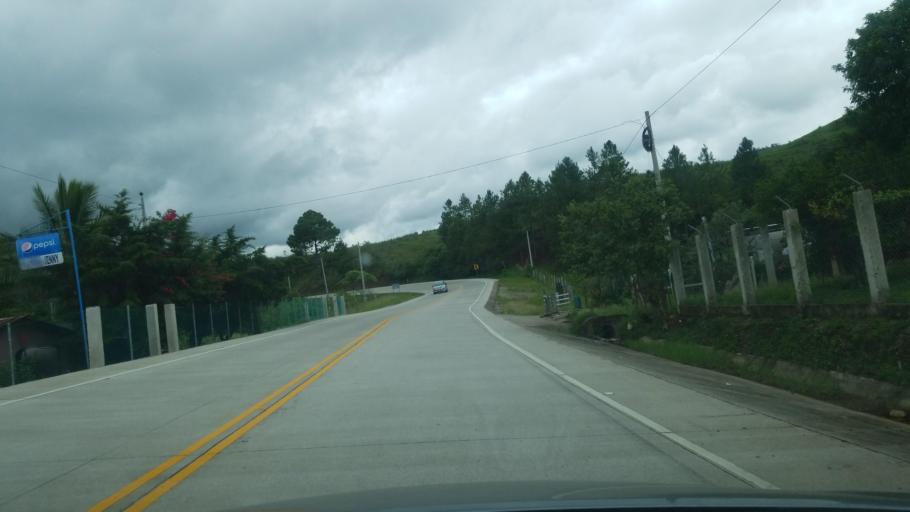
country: HN
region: Copan
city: San Jeronimo
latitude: 14.9401
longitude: -88.9166
